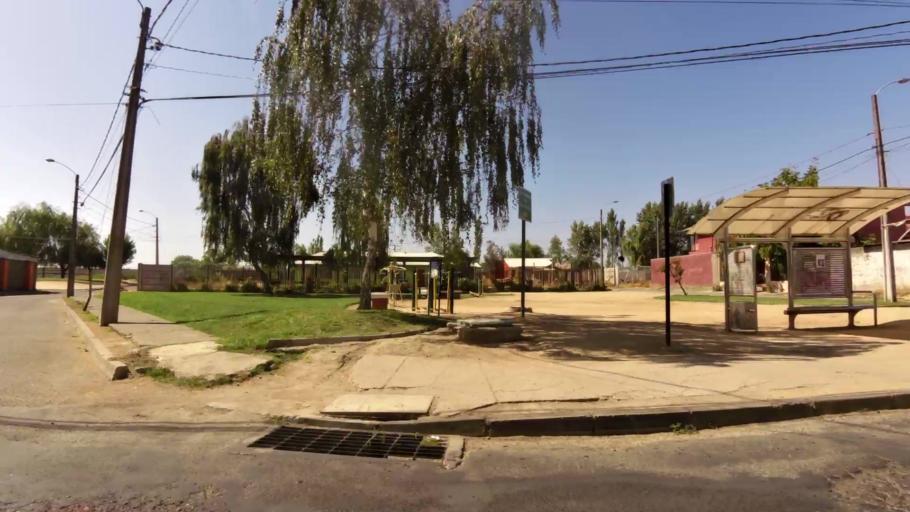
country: CL
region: Maule
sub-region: Provincia de Talca
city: Talca
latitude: -35.4117
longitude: -71.6381
